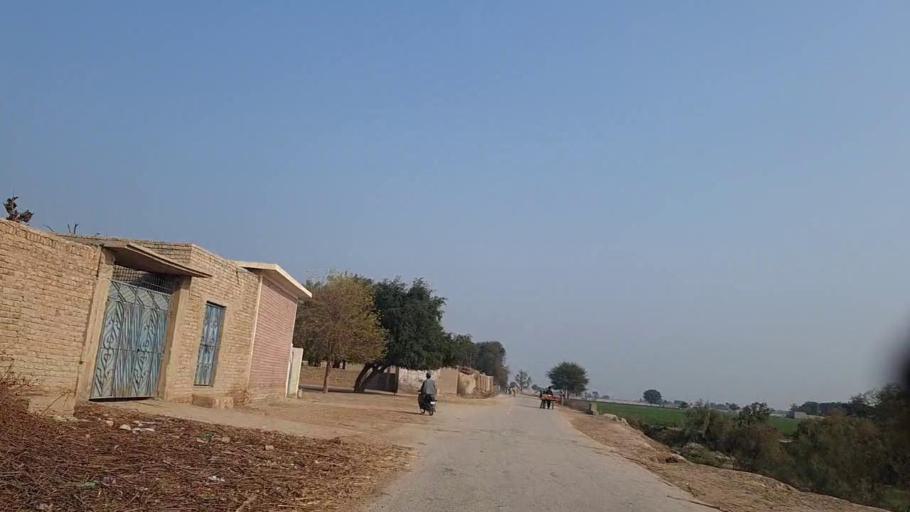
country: PK
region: Sindh
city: Sann
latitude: 26.1470
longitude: 68.1366
